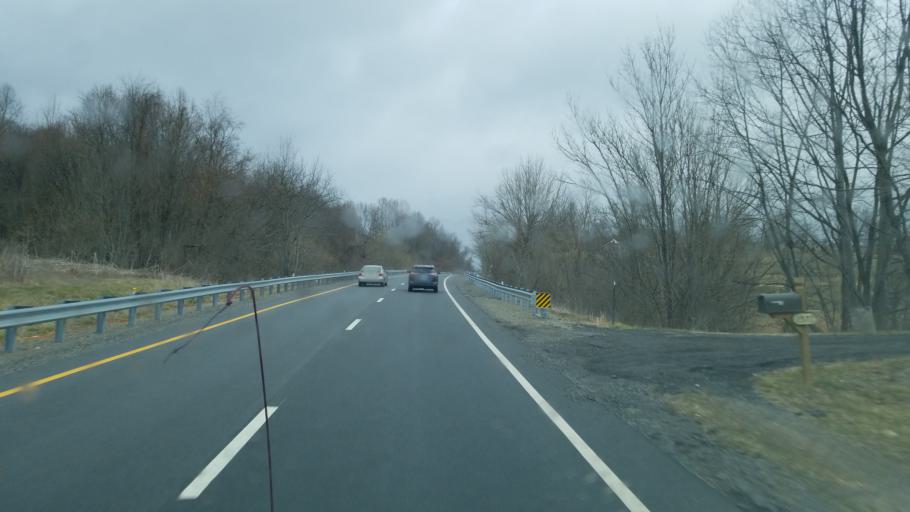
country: US
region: Virginia
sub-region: Giles County
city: Pearisburg
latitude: 37.2936
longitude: -80.7410
